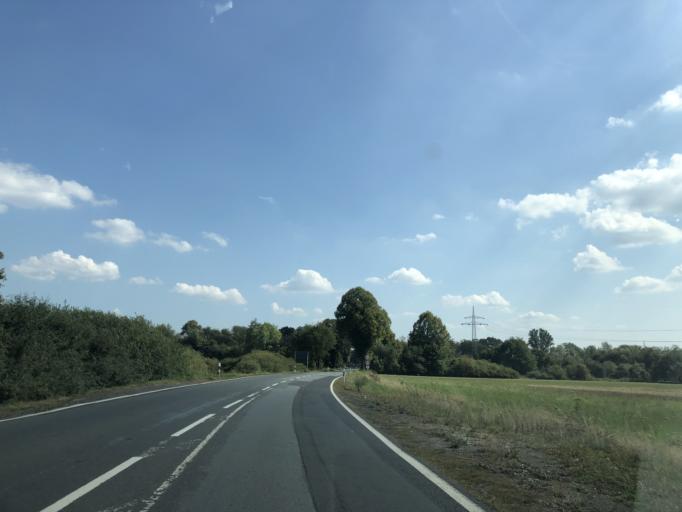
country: DE
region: Hesse
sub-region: Regierungsbezirk Giessen
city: Kirchhain
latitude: 50.8316
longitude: 8.9045
